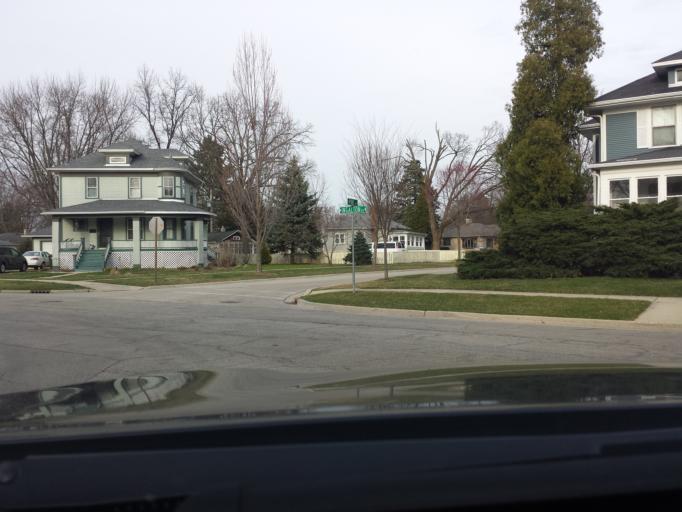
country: US
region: Illinois
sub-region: DuPage County
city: West Chicago
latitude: 41.8881
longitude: -88.1978
